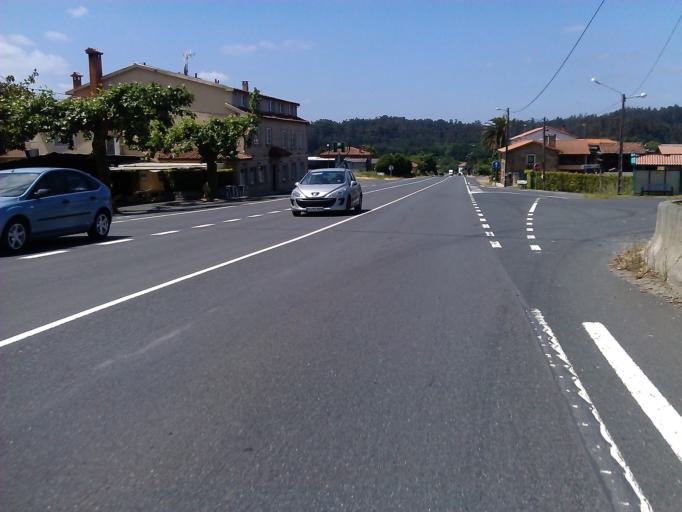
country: ES
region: Galicia
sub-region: Provincia da Coruna
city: Touro
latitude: 42.9167
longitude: -8.3507
